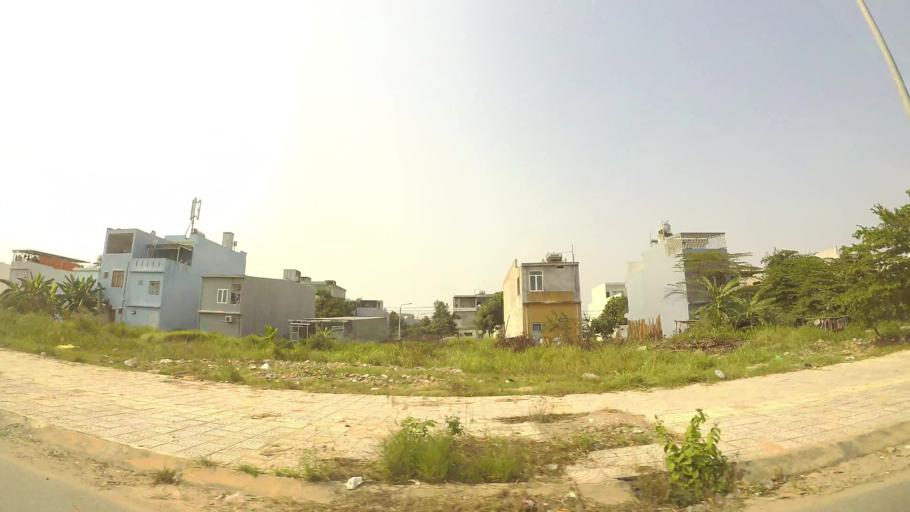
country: VN
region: Da Nang
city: Cam Le
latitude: 16.0096
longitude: 108.2033
